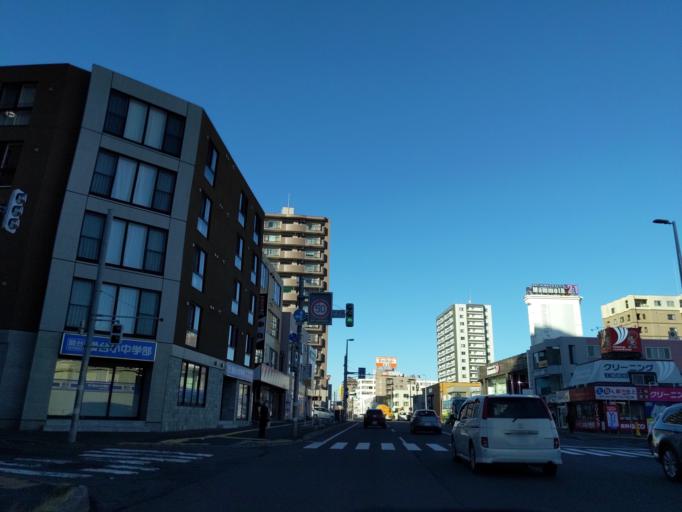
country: JP
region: Hokkaido
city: Sapporo
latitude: 43.0271
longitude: 141.3983
